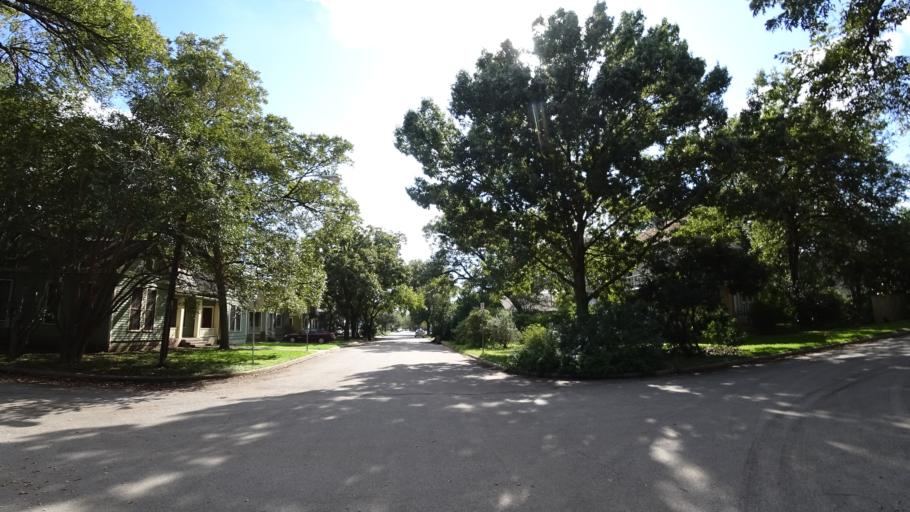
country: US
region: Texas
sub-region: Travis County
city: Austin
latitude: 30.3038
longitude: -97.7303
